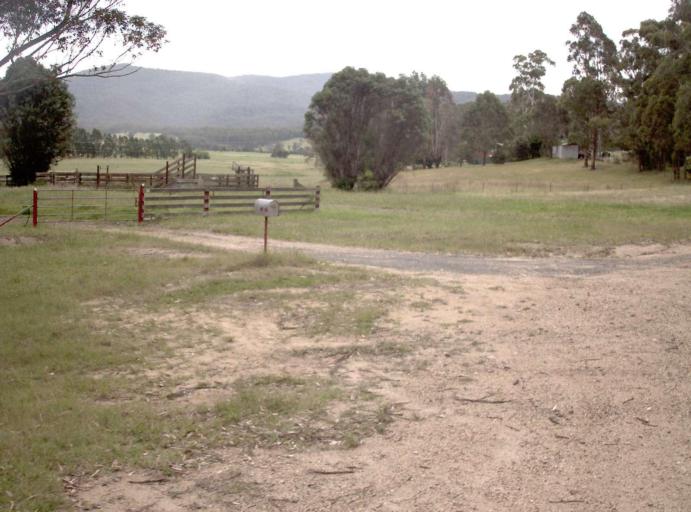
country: AU
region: New South Wales
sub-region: Bombala
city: Bombala
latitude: -37.4901
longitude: 149.1825
